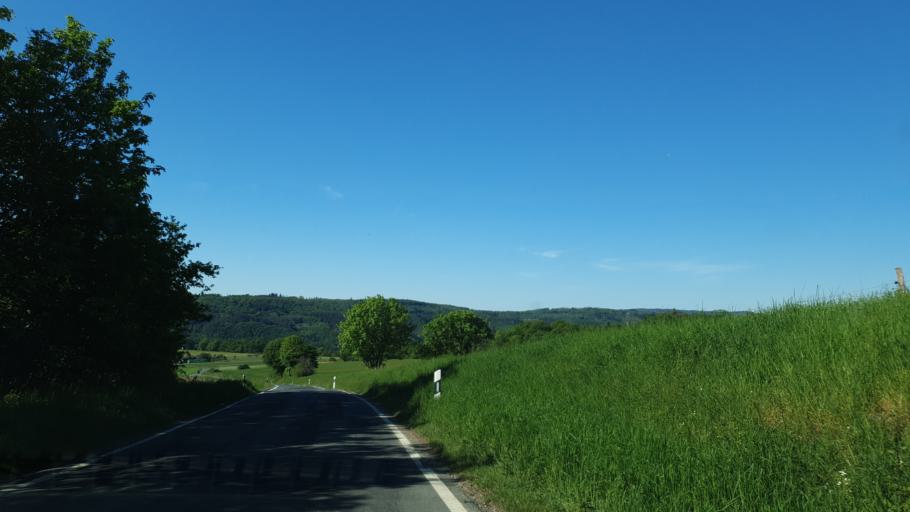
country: DE
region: Rheinland-Pfalz
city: Frucht
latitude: 50.3212
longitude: 7.6904
